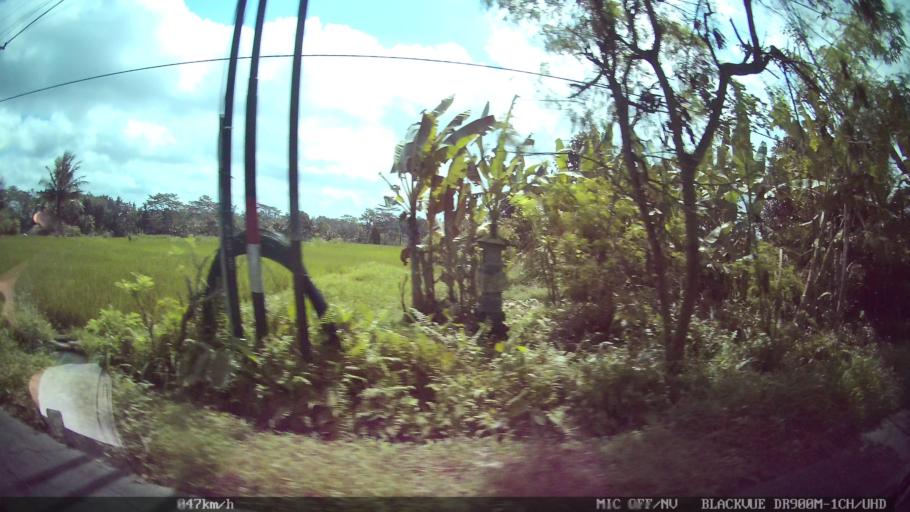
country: ID
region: Bali
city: Banjar Mulung
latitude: -8.5049
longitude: 115.3207
